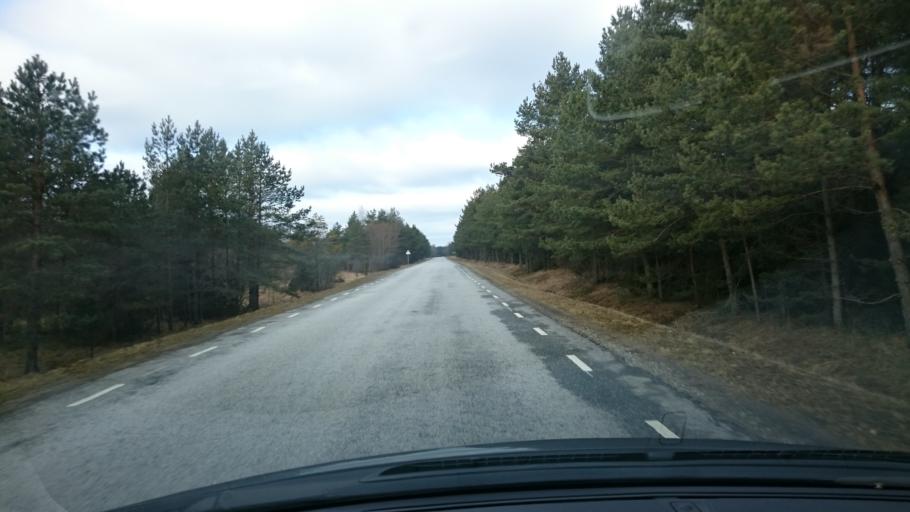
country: EE
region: Harju
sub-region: Keila linn
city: Keila
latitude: 59.3498
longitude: 24.3520
